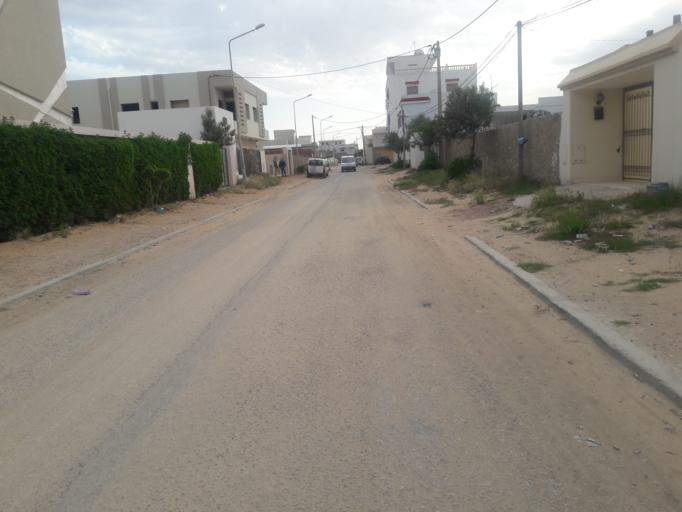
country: TN
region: Safaqis
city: Al Qarmadah
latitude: 34.8142
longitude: 10.7465
